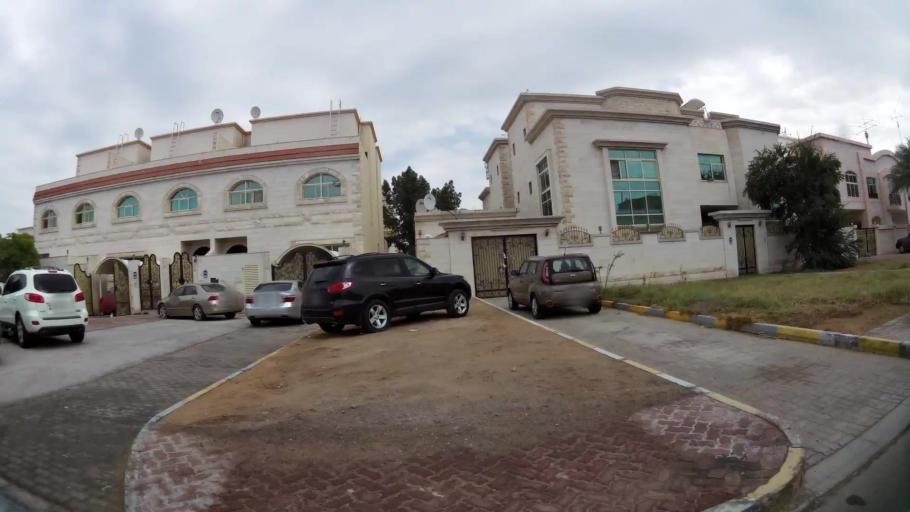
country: AE
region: Abu Dhabi
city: Abu Dhabi
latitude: 24.4332
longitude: 54.4070
